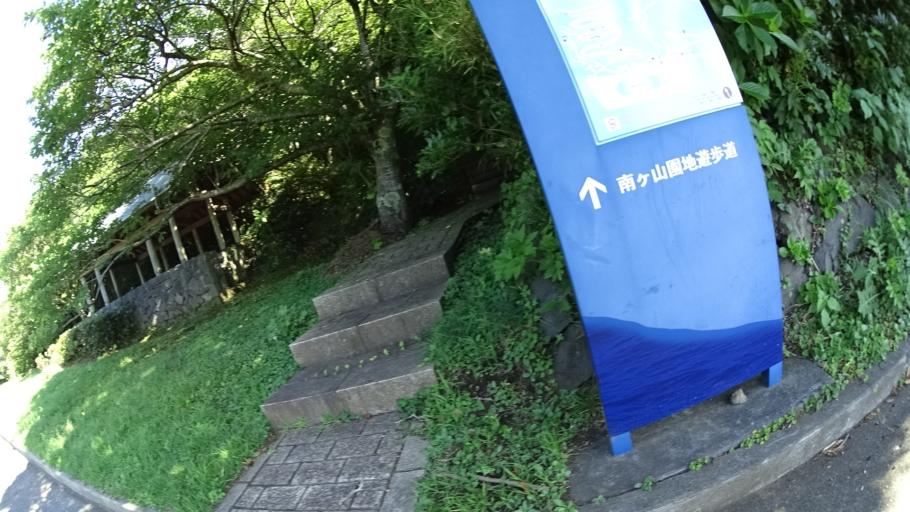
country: JP
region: Shizuoka
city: Shimoda
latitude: 34.5148
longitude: 139.2766
